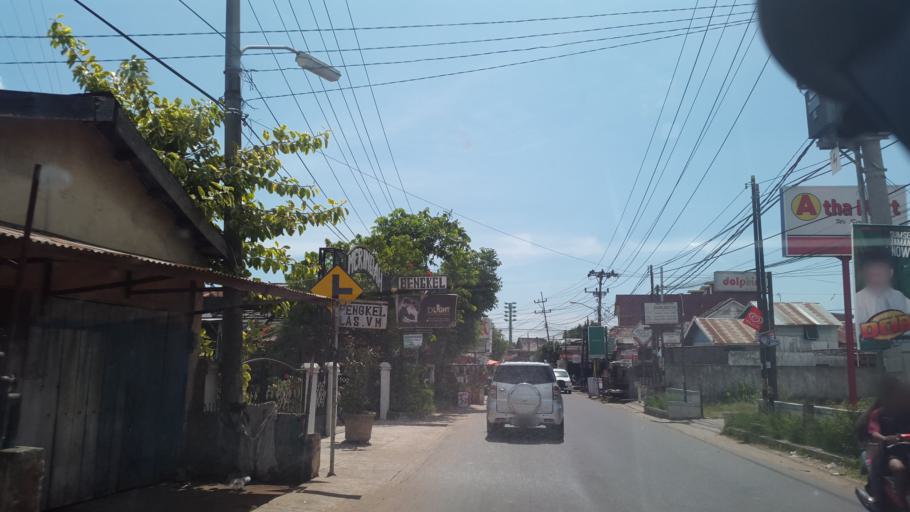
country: ID
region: South Sumatra
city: Plaju
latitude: -3.0021
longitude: 104.7298
